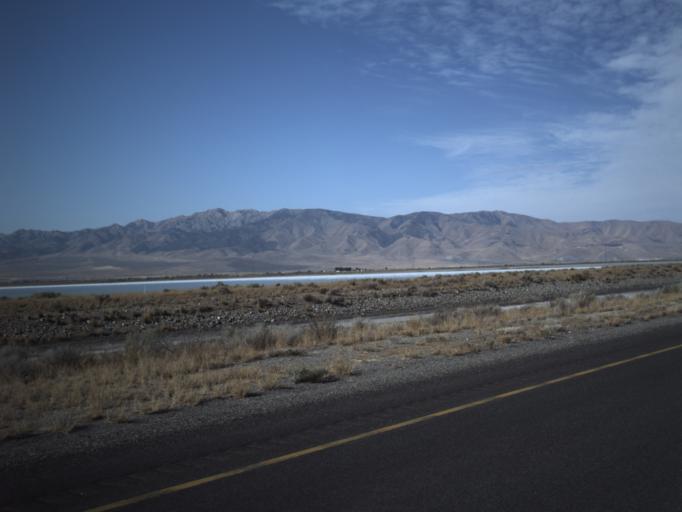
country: US
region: Utah
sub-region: Tooele County
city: Grantsville
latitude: 40.6747
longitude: -112.3977
